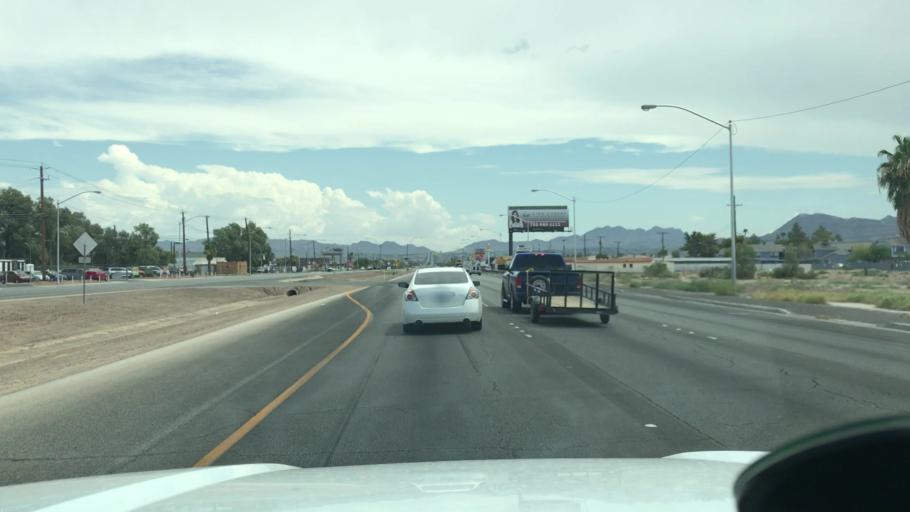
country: US
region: Nevada
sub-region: Clark County
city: Whitney
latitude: 36.0943
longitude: -115.0437
